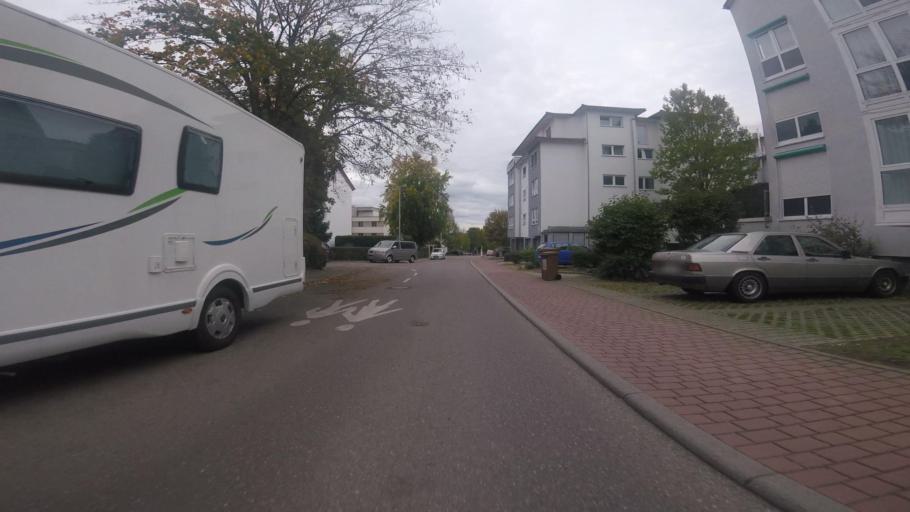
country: DE
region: Baden-Wuerttemberg
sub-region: Regierungsbezirk Stuttgart
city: Backnang
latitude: 48.9536
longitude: 9.4204
